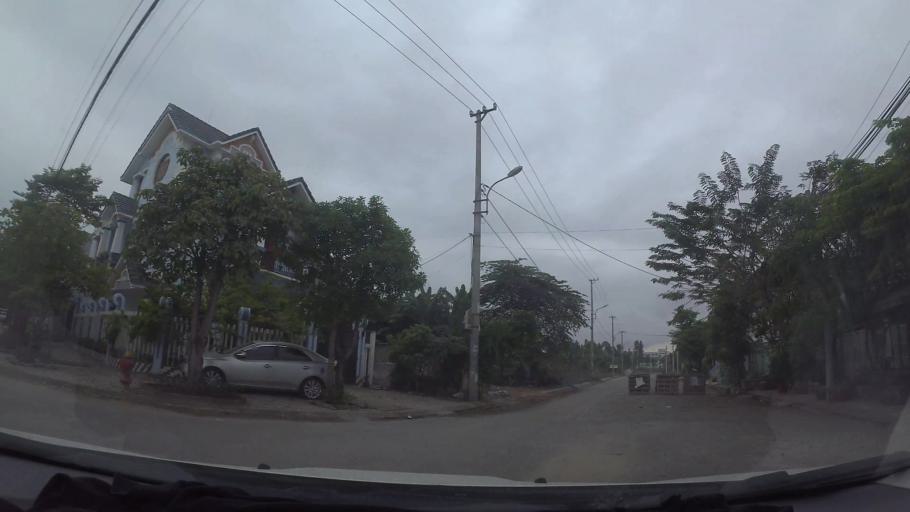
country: VN
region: Da Nang
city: Lien Chieu
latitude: 16.0660
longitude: 108.1589
